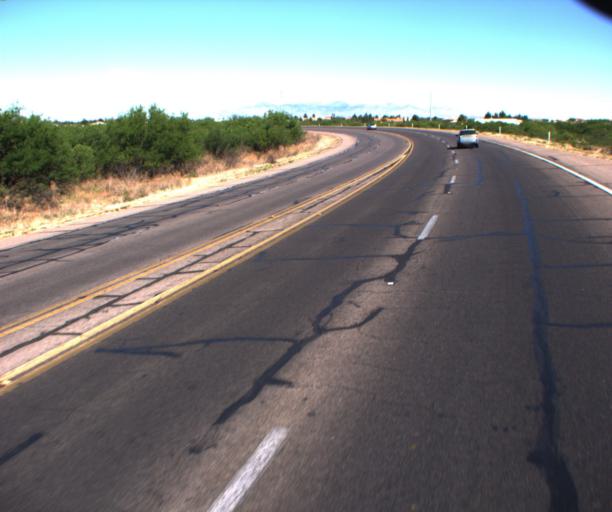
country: US
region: Arizona
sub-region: Cochise County
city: Sierra Vista
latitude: 31.5665
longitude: -110.2574
